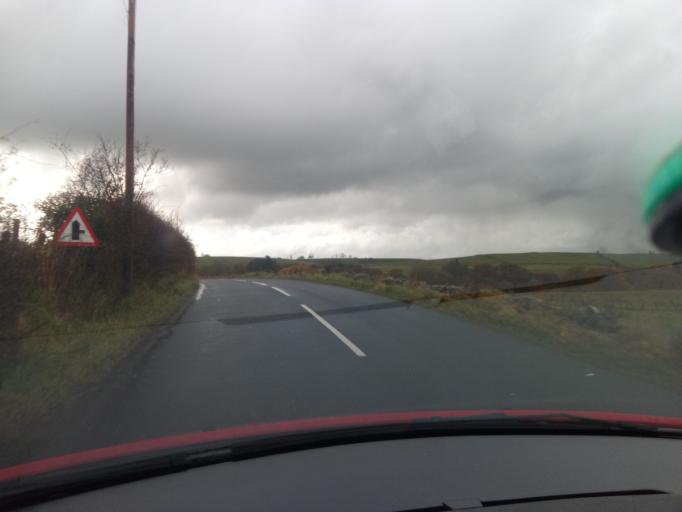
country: GB
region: England
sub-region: Northumberland
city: Birtley
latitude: 55.1112
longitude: -2.2408
